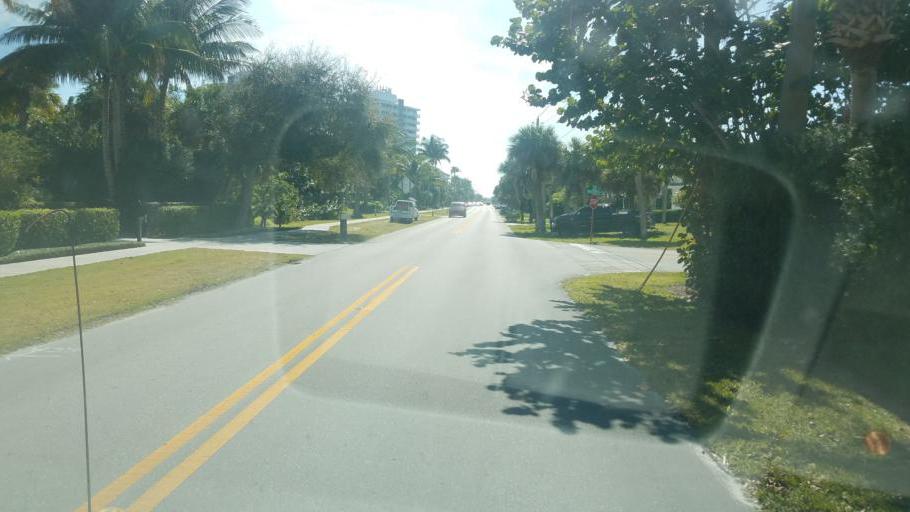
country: US
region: Florida
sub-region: Indian River County
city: Vero Beach
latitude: 27.6587
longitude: -80.3581
